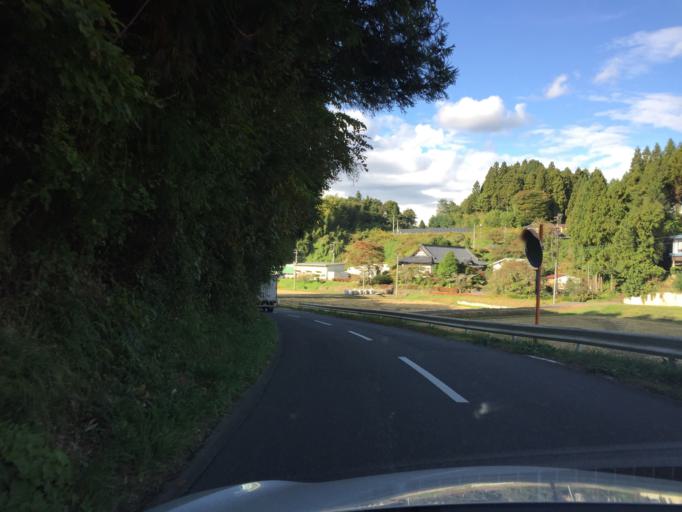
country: JP
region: Fukushima
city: Ishikawa
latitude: 37.2284
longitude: 140.4530
